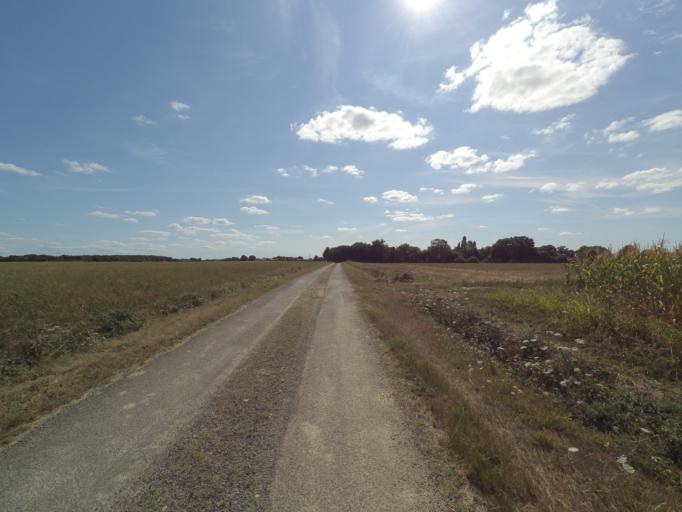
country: FR
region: Pays de la Loire
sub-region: Departement de la Loire-Atlantique
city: Vieillevigne
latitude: 46.9598
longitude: -1.4490
